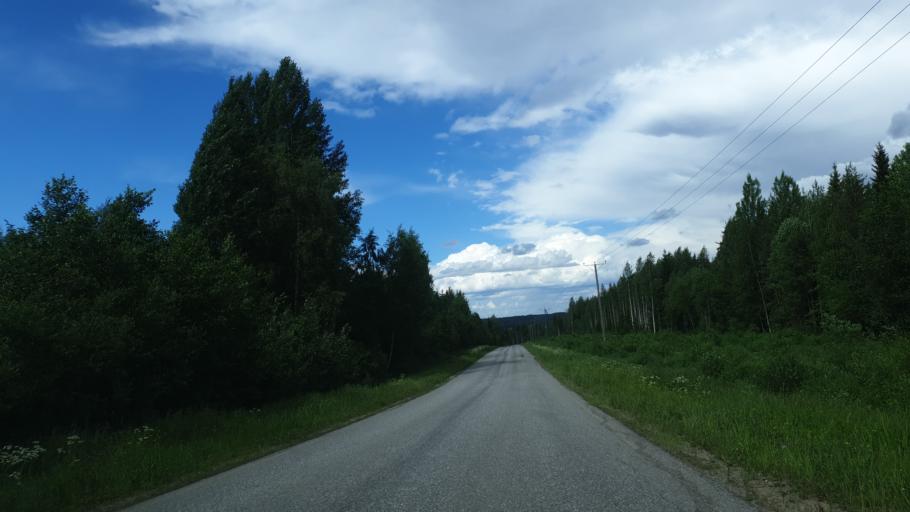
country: FI
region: Northern Savo
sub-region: Koillis-Savo
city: Kaavi
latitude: 62.9765
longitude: 28.7488
